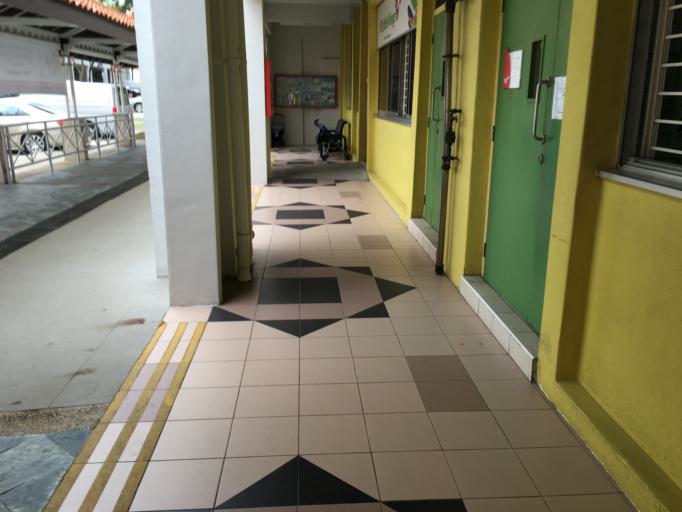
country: SG
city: Singapore
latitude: 1.3414
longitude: 103.7370
